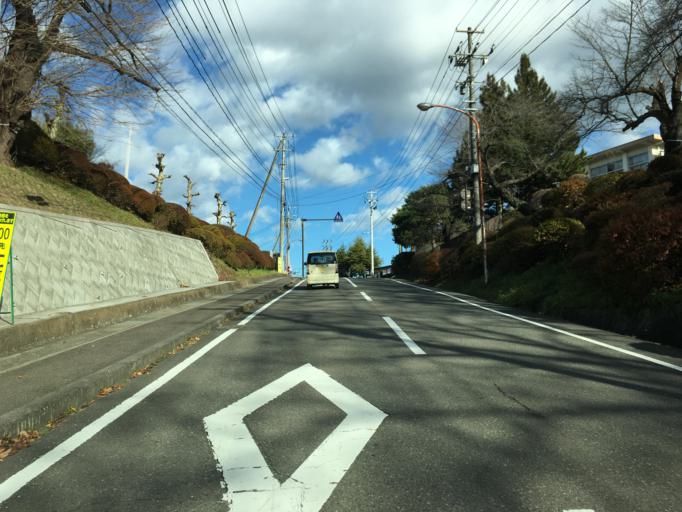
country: JP
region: Fukushima
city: Nihommatsu
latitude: 37.5934
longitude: 140.4498
